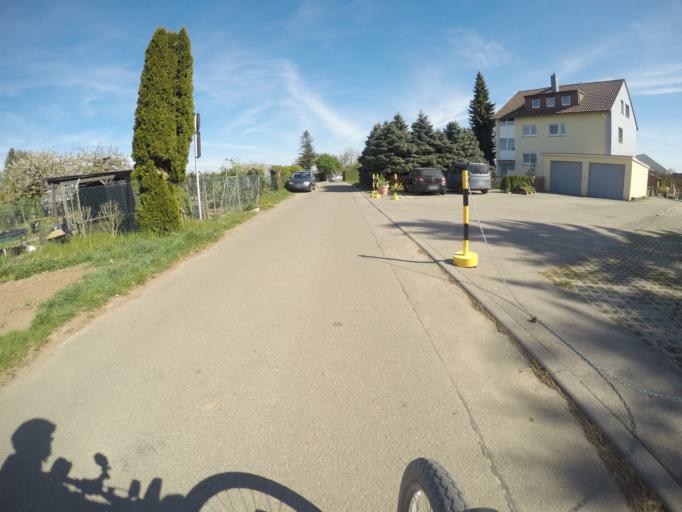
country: DE
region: Baden-Wuerttemberg
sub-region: Regierungsbezirk Stuttgart
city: Kornwestheim
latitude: 48.8681
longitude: 9.1726
